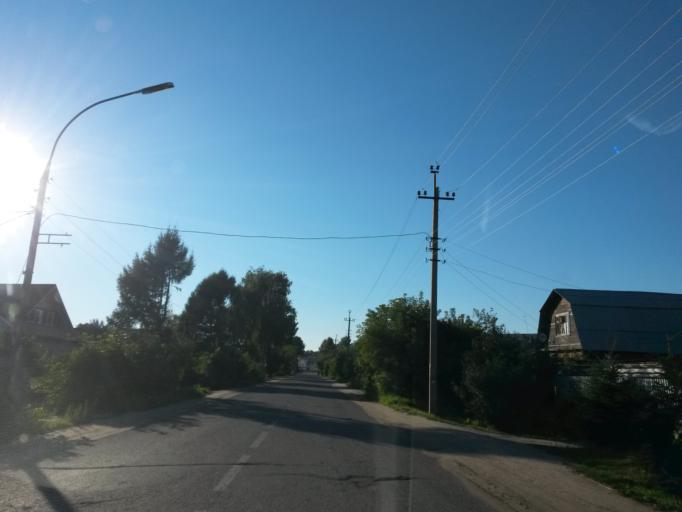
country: RU
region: Jaroslavl
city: Gavrilov-Yam
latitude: 57.2972
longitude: 39.8715
